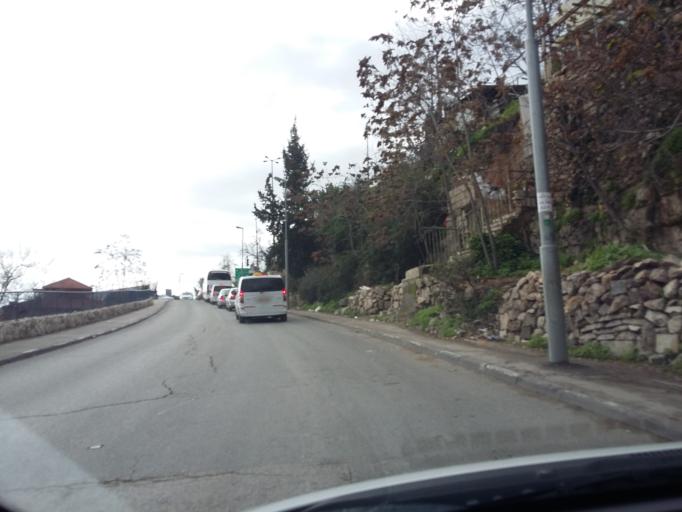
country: PS
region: West Bank
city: East Jerusalem
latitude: 31.7849
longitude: 35.2372
